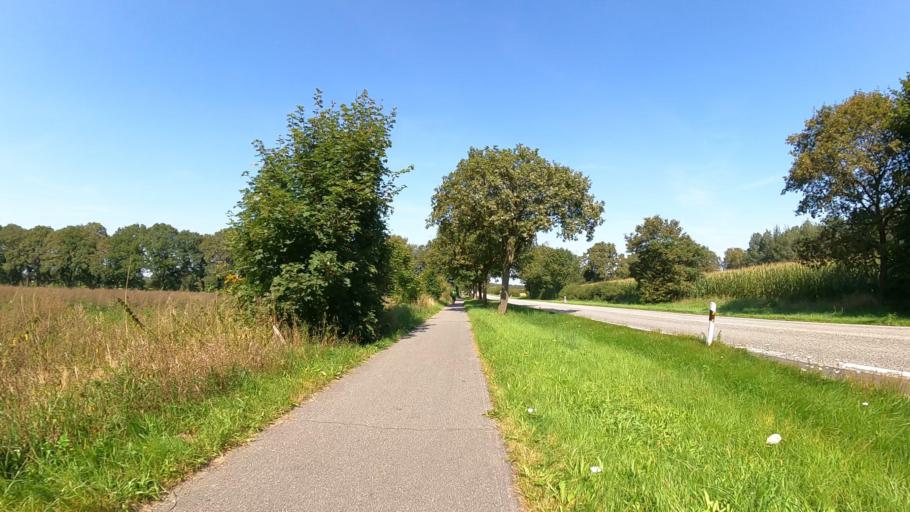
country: DE
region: Schleswig-Holstein
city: Lentfohrden
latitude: 53.8846
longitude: 9.8864
